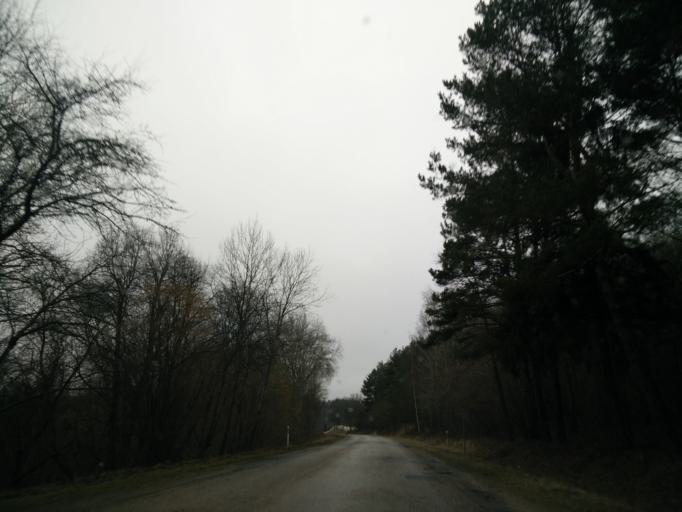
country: LT
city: Ariogala
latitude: 55.2952
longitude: 23.4418
